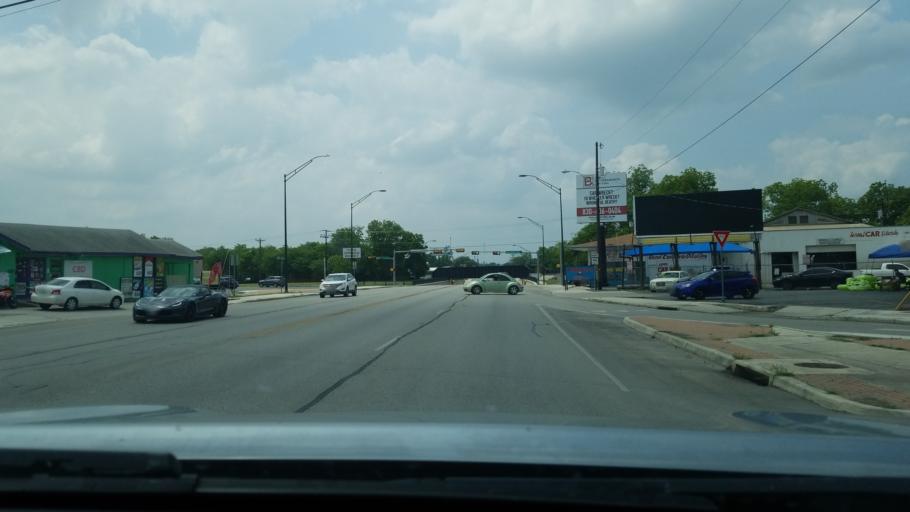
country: US
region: Texas
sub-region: Comal County
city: New Braunfels
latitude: 29.6948
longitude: -98.1126
